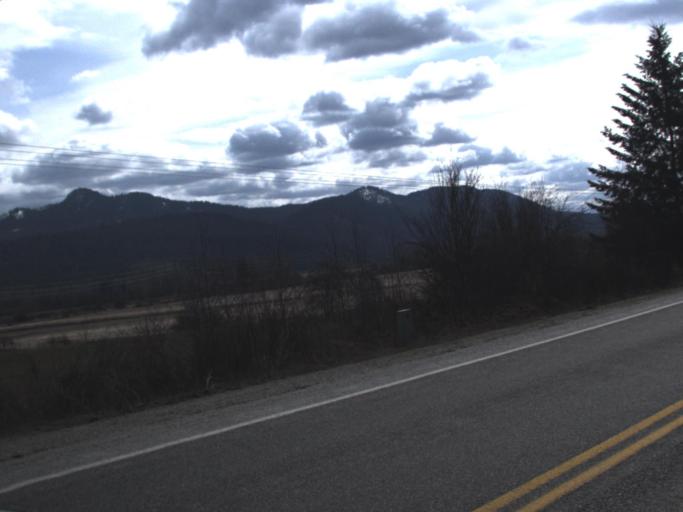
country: US
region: Washington
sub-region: Pend Oreille County
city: Newport
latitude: 48.4118
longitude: -117.3132
